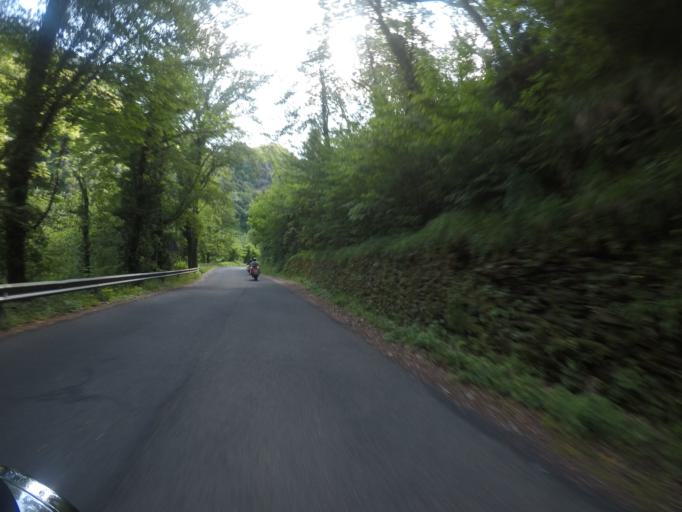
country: IT
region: Tuscany
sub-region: Provincia di Massa-Carrara
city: Montignoso
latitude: 44.0522
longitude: 10.1893
